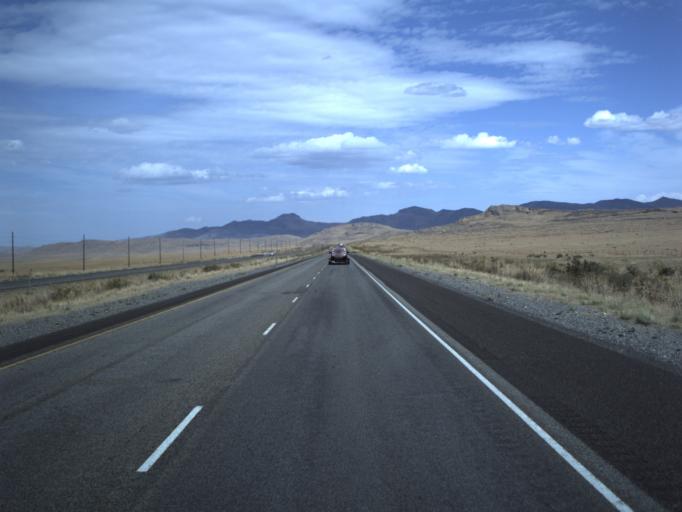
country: US
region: Utah
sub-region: Tooele County
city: Grantsville
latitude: 40.7899
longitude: -112.9559
